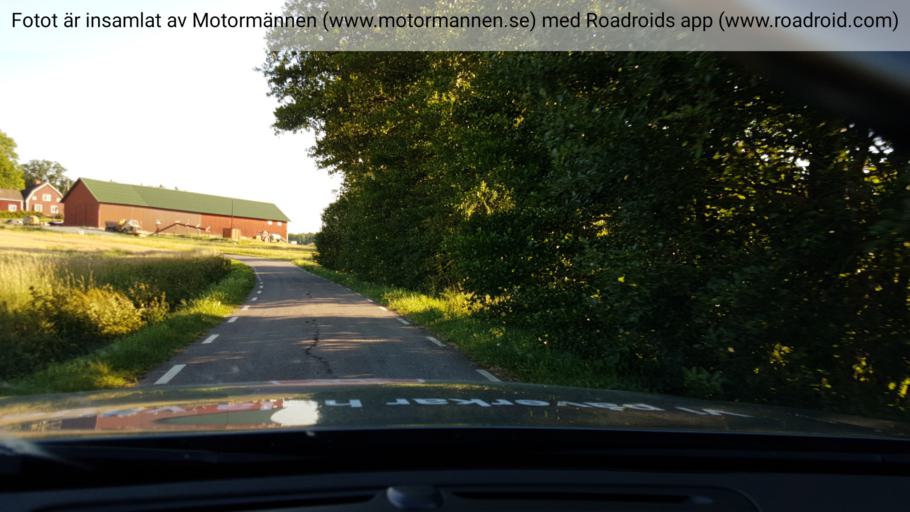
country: SE
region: Vaestmanland
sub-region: Kopings Kommun
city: Koping
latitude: 59.6346
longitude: 16.0618
